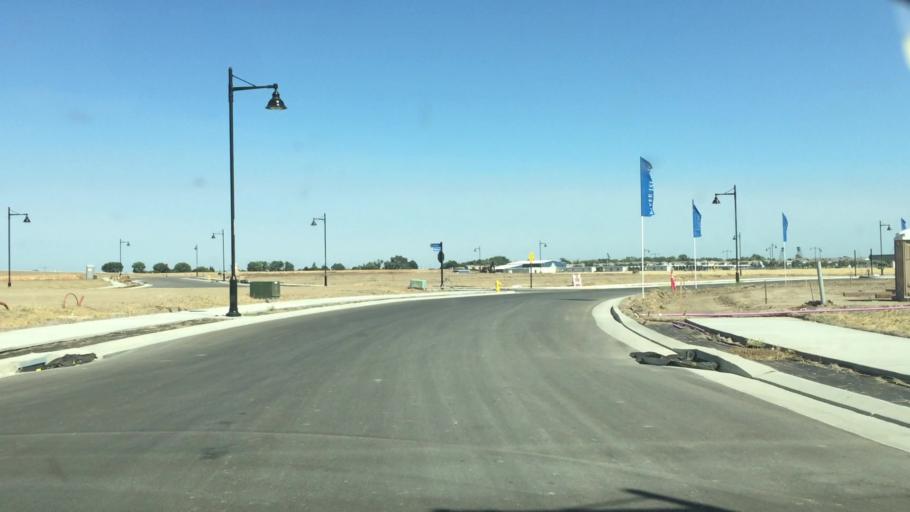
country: US
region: California
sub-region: San Joaquin County
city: Lathrop
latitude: 37.8037
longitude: -121.3252
